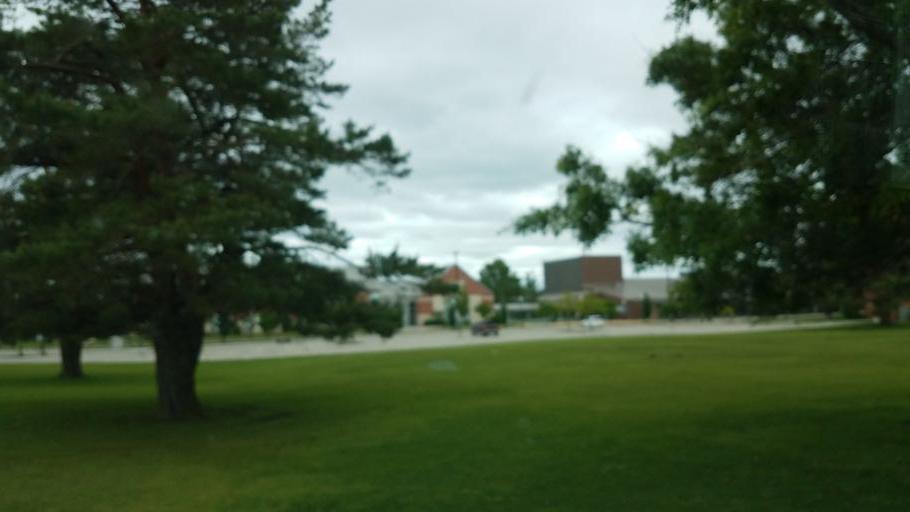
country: US
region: Iowa
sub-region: Decatur County
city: Lamoni
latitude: 40.6175
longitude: -93.9236
